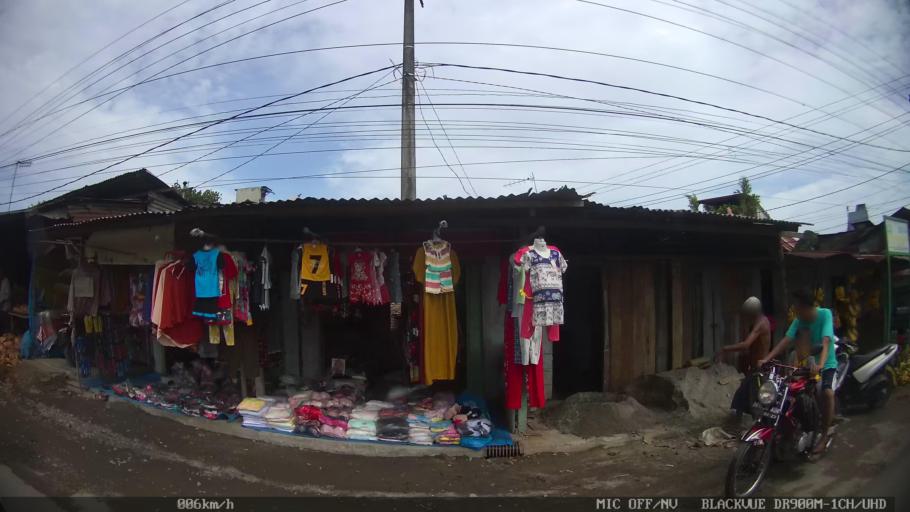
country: ID
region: North Sumatra
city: Percut
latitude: 3.6128
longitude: 98.8025
